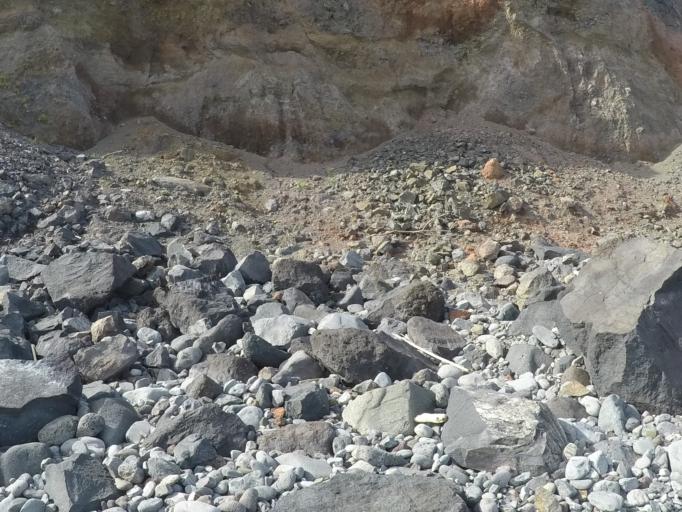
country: PT
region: Madeira
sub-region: Sao Vicente
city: Sao Vicente
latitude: 32.8101
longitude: -16.9698
